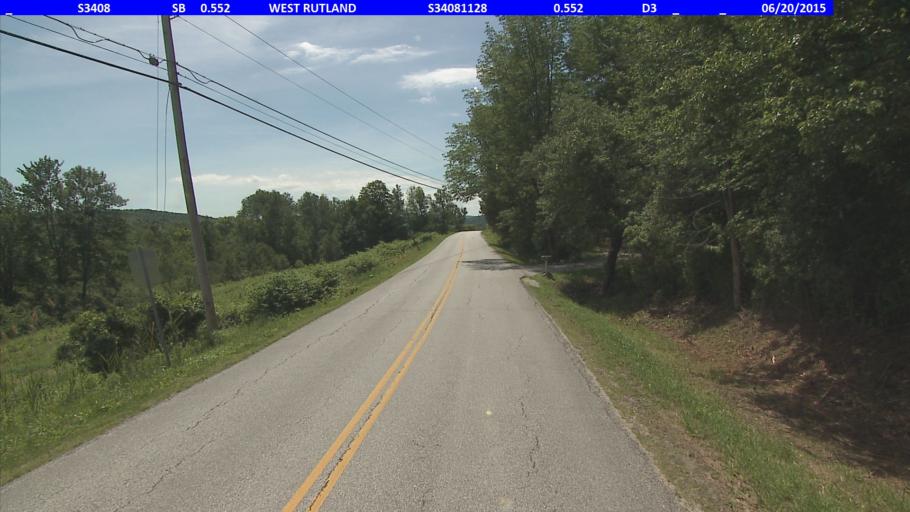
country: US
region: Vermont
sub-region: Rutland County
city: West Rutland
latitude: 43.6180
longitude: -73.0645
